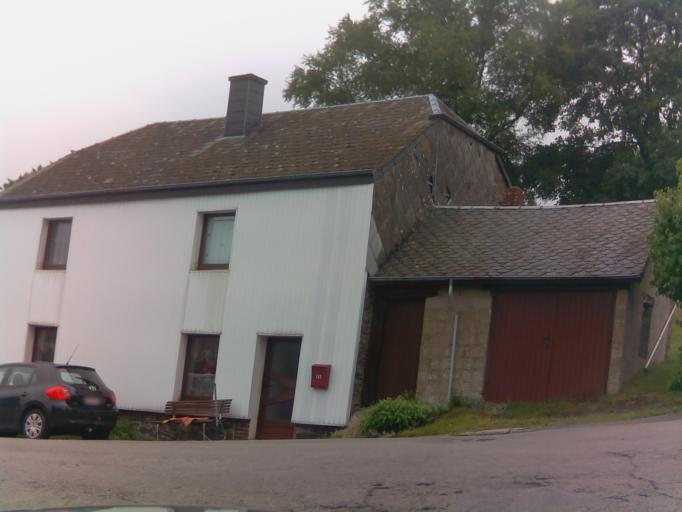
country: BE
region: Wallonia
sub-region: Province du Luxembourg
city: Libin
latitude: 49.9237
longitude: 5.2818
